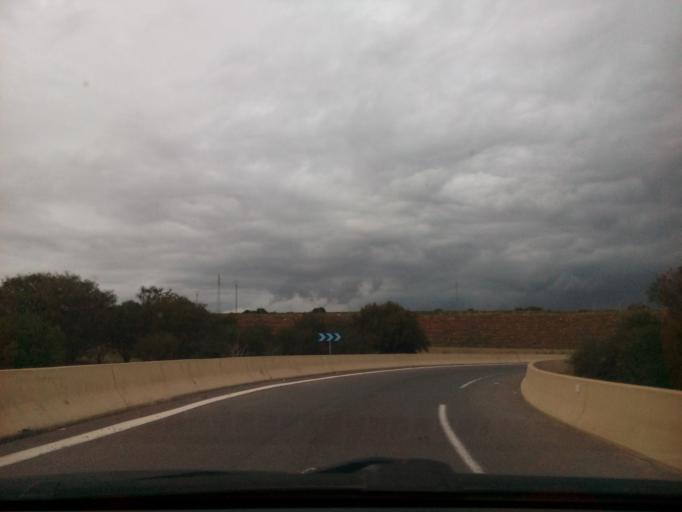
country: DZ
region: Oran
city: Sidi ech Chahmi
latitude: 35.5446
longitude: -0.3799
